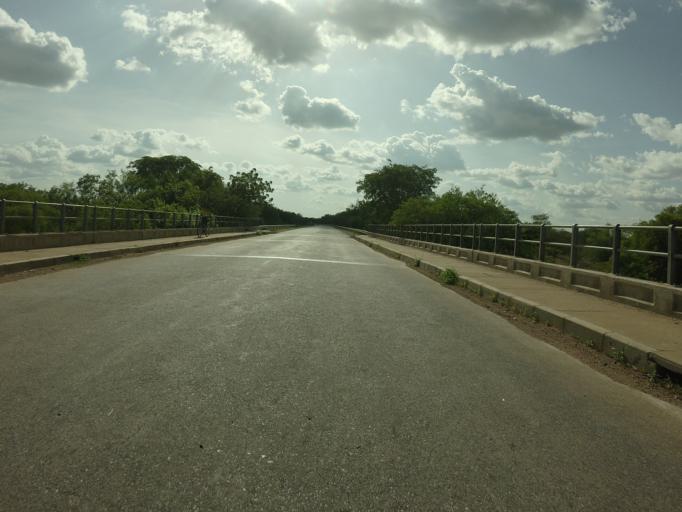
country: GH
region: Upper East
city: Bolgatanga
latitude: 10.5836
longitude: -0.8345
